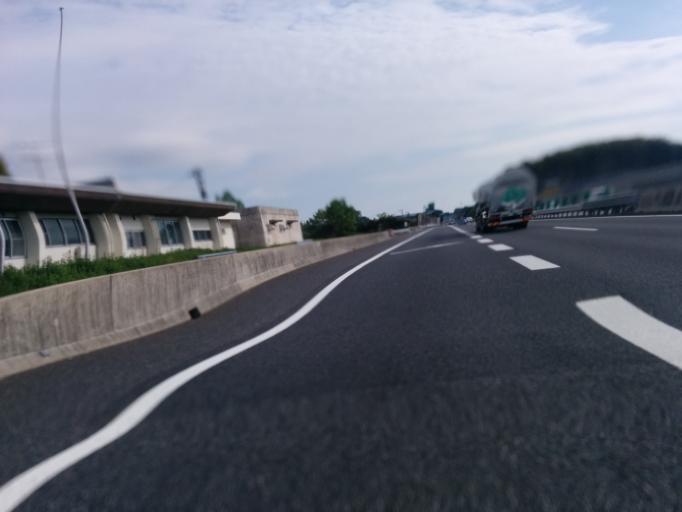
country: JP
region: Mie
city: Kameyama
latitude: 34.9121
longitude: 136.4760
